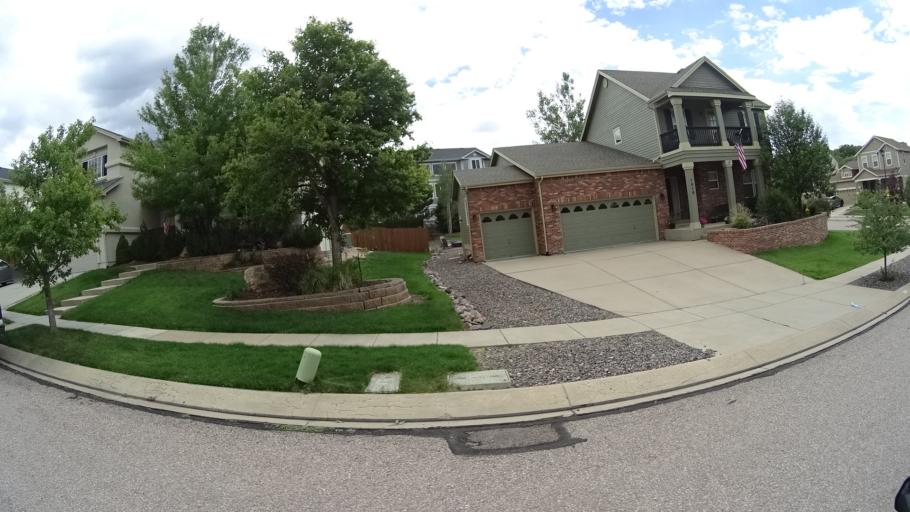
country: US
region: Colorado
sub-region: El Paso County
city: Gleneagle
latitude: 39.0330
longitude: -104.8107
